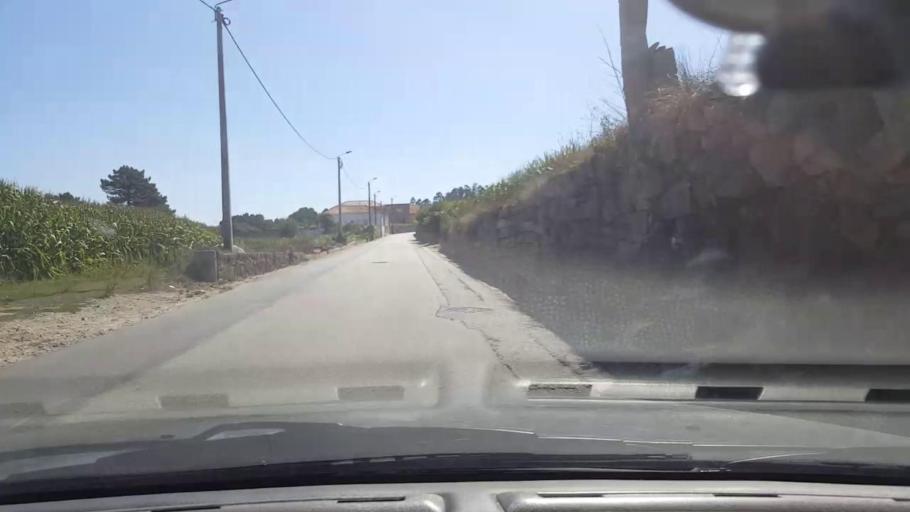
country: PT
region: Porto
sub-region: Matosinhos
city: Lavra
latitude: 41.2658
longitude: -8.6912
